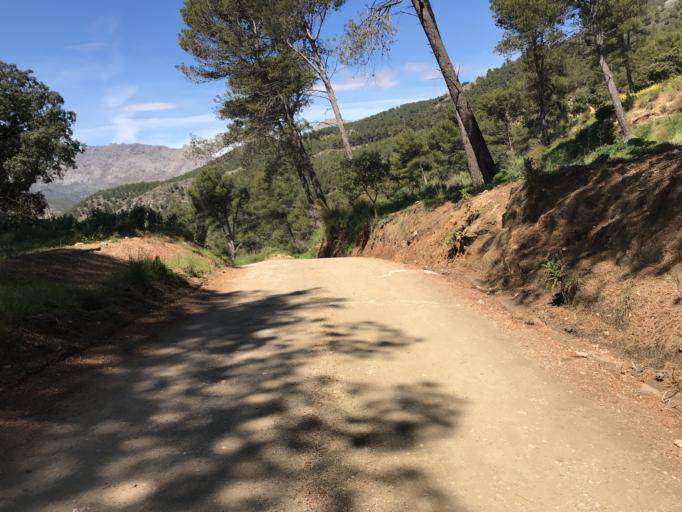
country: ES
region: Andalusia
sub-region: Provincia de Malaga
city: Alcaucin
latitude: 36.9189
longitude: -4.0904
